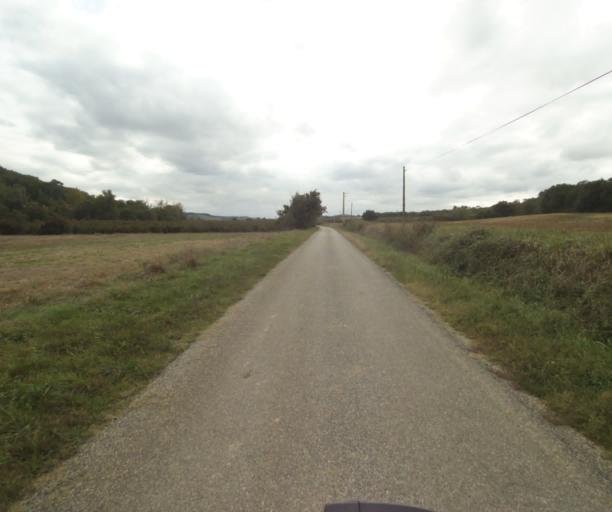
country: FR
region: Midi-Pyrenees
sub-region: Departement du Tarn-et-Garonne
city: Beaumont-de-Lomagne
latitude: 43.8320
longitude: 1.0963
